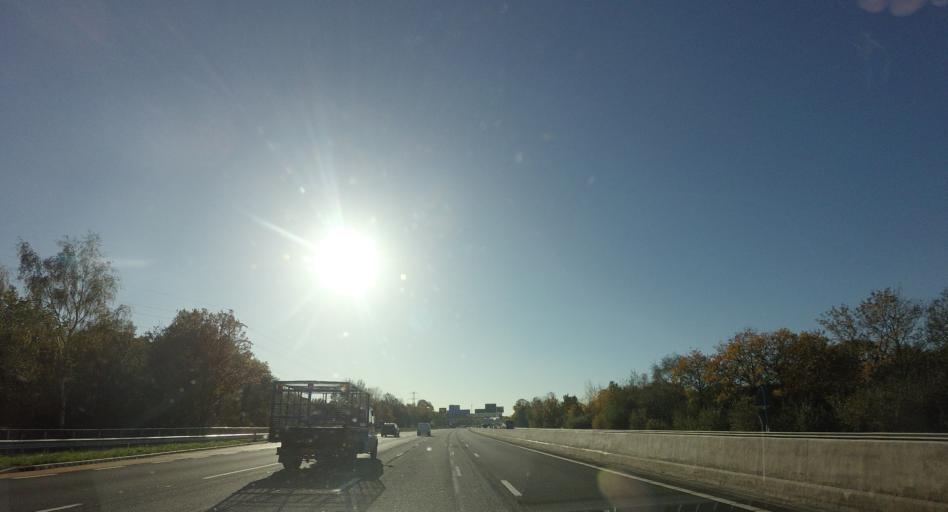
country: GB
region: England
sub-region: West Sussex
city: Copthorne
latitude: 51.1474
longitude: -0.1364
